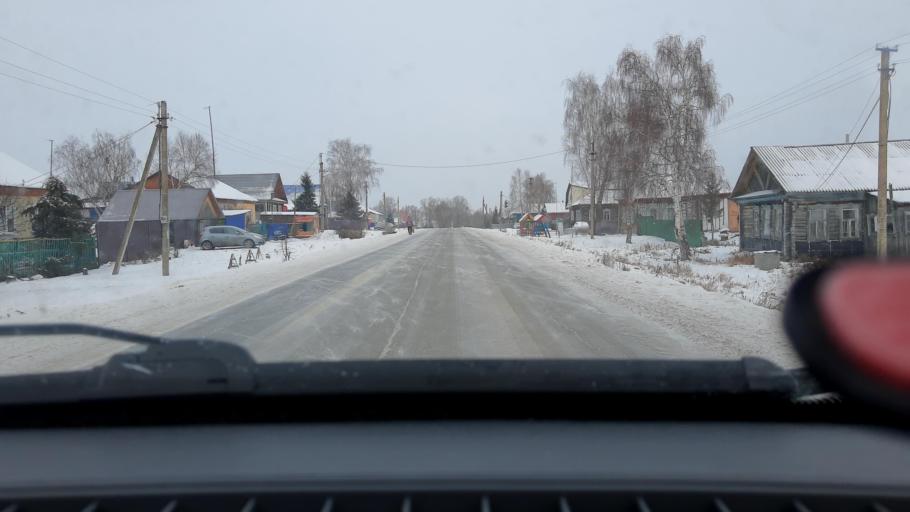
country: RU
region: Bashkortostan
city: Iglino
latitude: 54.7370
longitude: 56.3965
